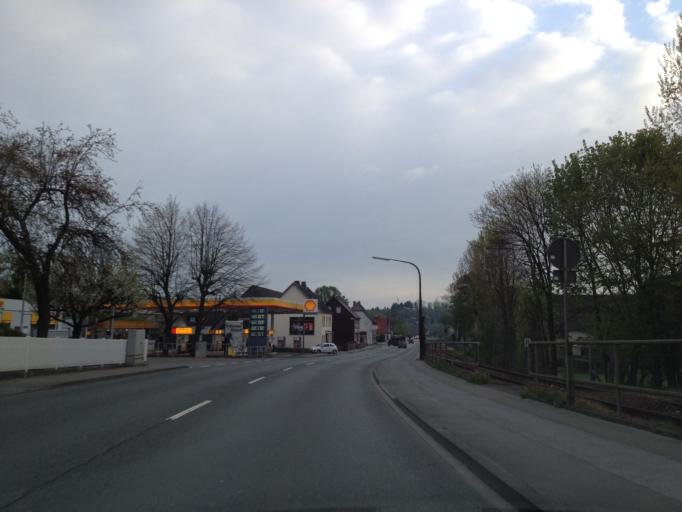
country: DE
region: North Rhine-Westphalia
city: Warstein
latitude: 51.4807
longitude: 8.3347
